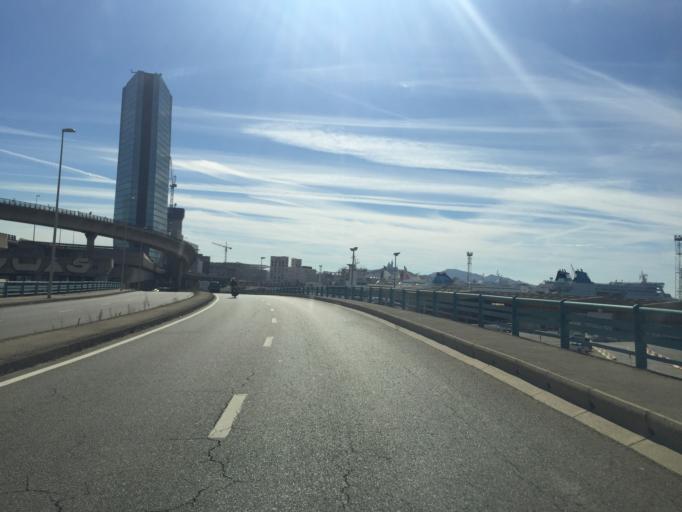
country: FR
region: Provence-Alpes-Cote d'Azur
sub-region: Departement des Bouches-du-Rhone
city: Marseille 03
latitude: 43.3184
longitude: 5.3626
